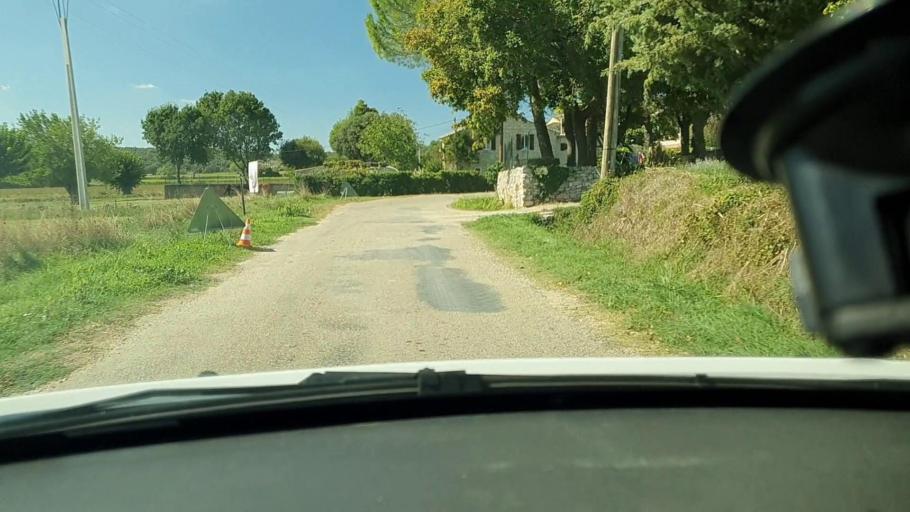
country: FR
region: Languedoc-Roussillon
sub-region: Departement du Gard
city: Goudargues
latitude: 44.1737
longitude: 4.3762
